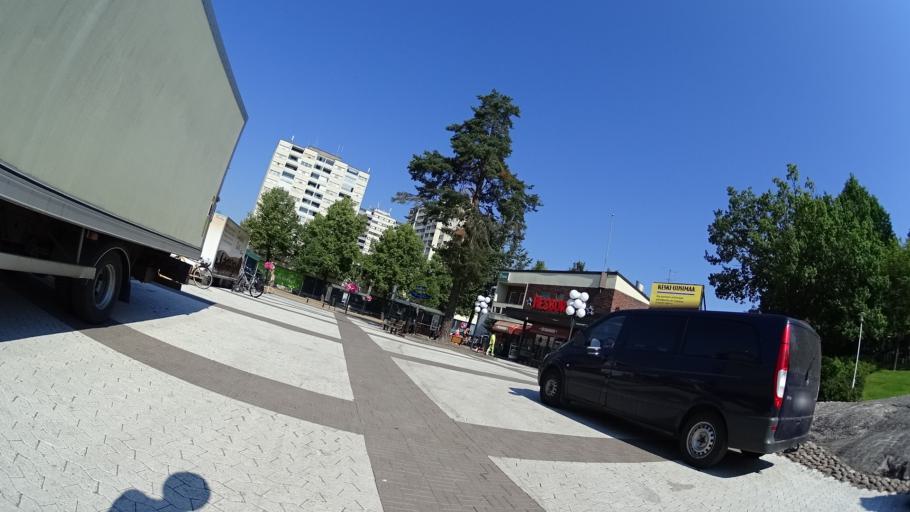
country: FI
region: Uusimaa
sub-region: Helsinki
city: Kerava
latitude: 60.4031
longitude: 25.1018
